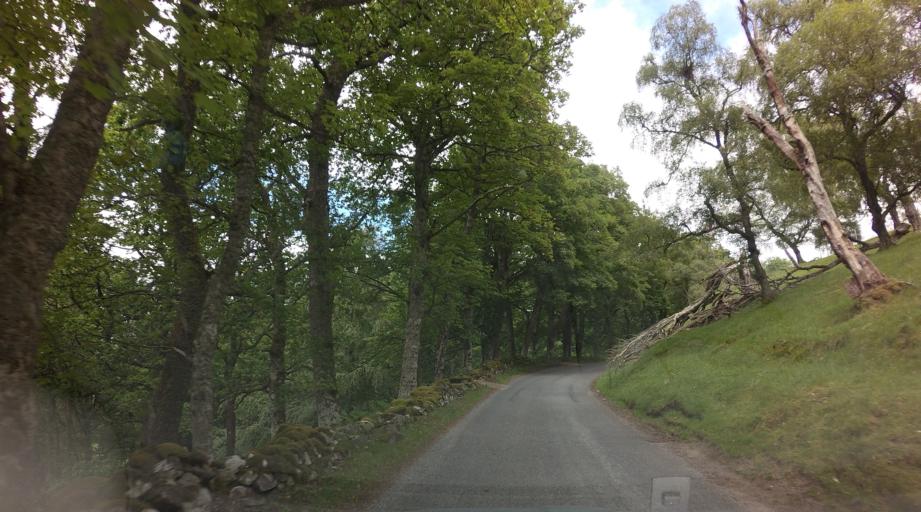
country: GB
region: Scotland
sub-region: Perth and Kinross
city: Aberfeldy
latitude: 56.6924
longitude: -4.1109
